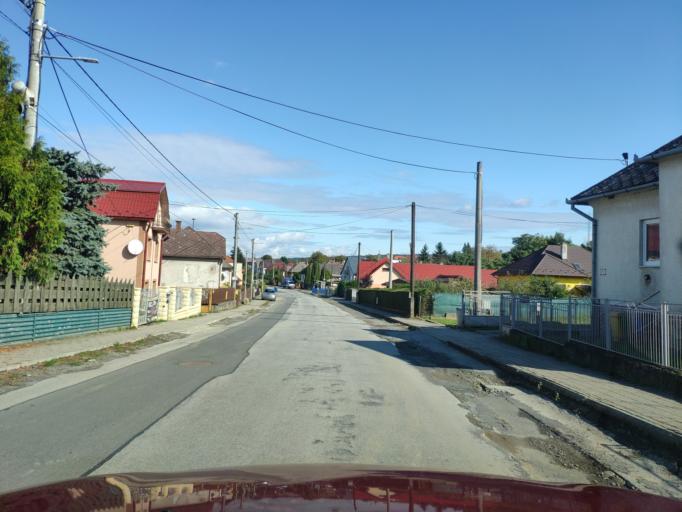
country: SK
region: Presovsky
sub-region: Okres Presov
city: Presov
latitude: 48.9125
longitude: 21.2594
